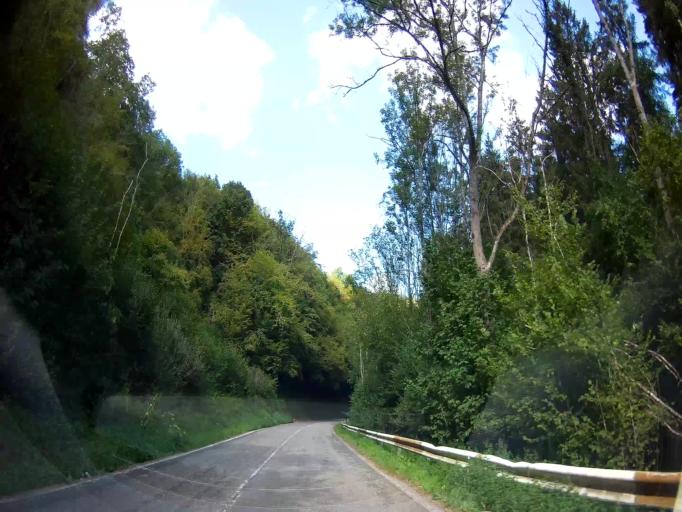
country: BE
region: Wallonia
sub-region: Province de Namur
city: Houyet
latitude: 50.2167
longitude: 4.9731
